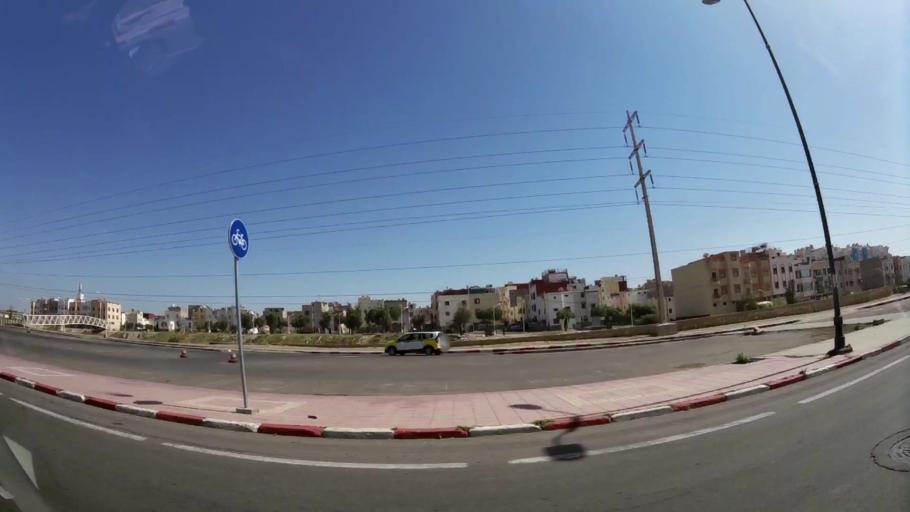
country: MA
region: Souss-Massa-Draa
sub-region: Agadir-Ida-ou-Tnan
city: Agadir
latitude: 30.4110
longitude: -9.5803
